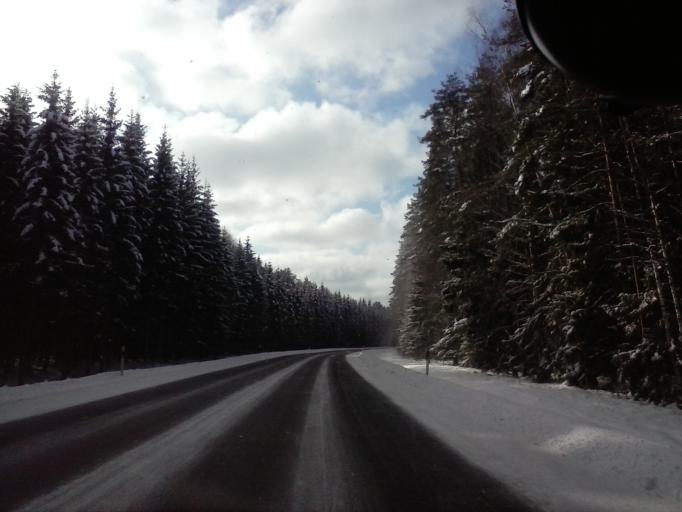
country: EE
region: Viljandimaa
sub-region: Moisakuela linn
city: Moisakula
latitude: 58.2243
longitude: 25.1060
